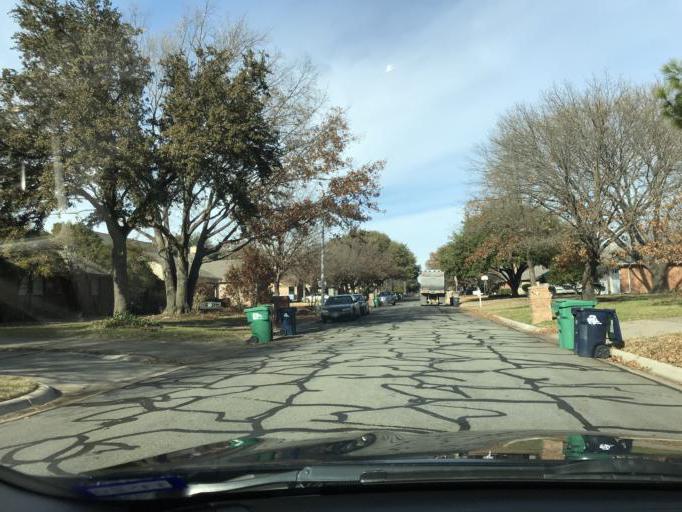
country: US
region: Texas
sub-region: Denton County
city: Denton
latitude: 33.2335
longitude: -97.1525
